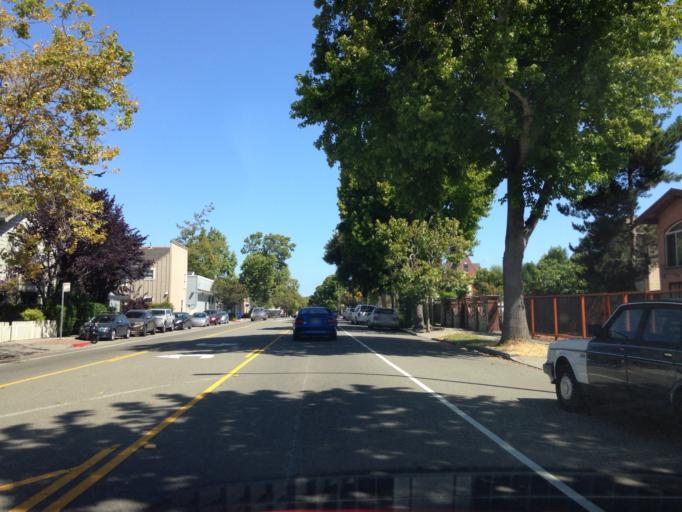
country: US
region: California
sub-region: Alameda County
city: Albany
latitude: 37.8697
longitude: -122.2983
